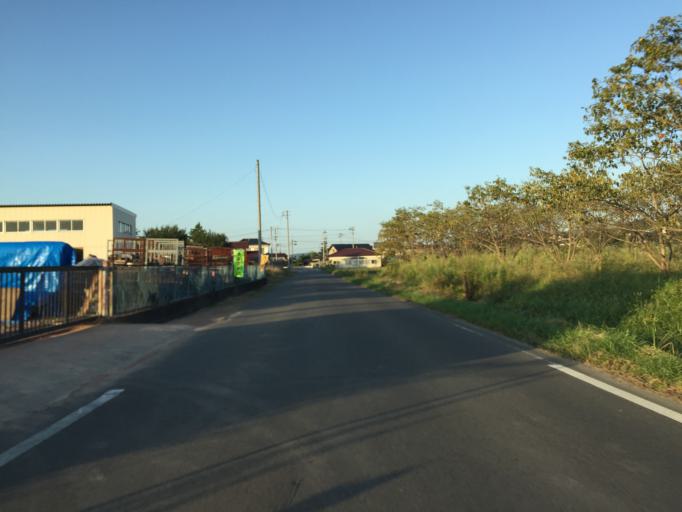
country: JP
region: Fukushima
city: Yanagawamachi-saiwaicho
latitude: 37.8259
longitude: 140.5916
